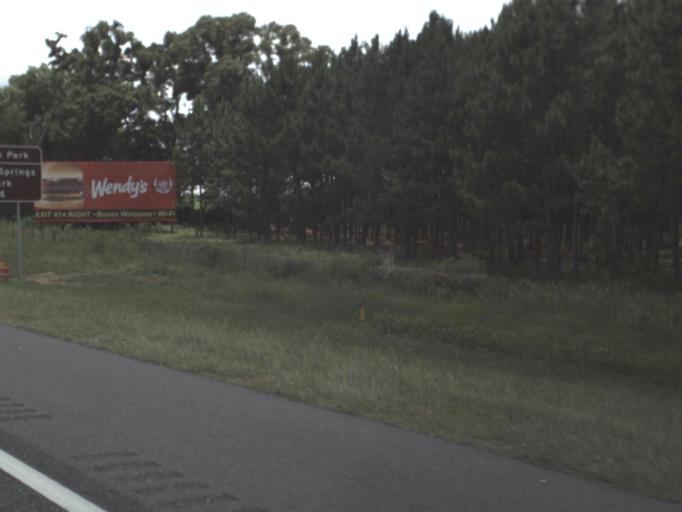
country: US
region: Florida
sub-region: Columbia County
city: Watertown
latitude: 30.0119
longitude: -82.6065
